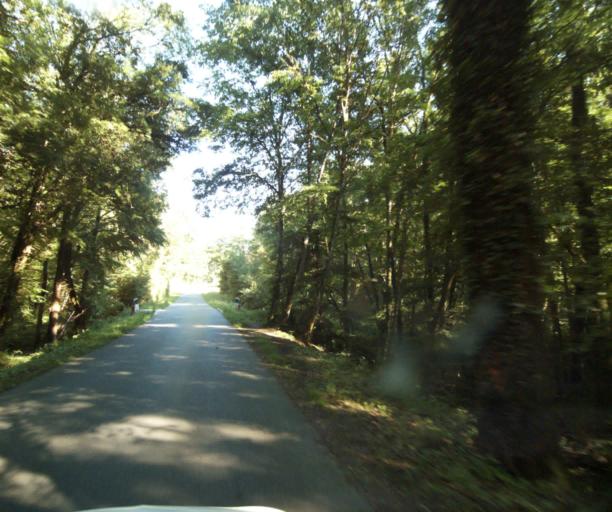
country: FR
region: Rhone-Alpes
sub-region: Departement de la Haute-Savoie
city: Massongy
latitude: 46.3341
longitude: 6.3277
